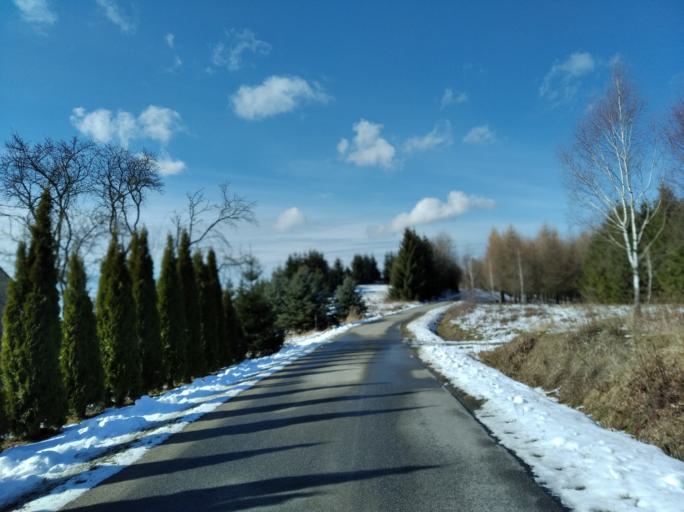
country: PL
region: Subcarpathian Voivodeship
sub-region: Powiat krosnienski
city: Korczyna
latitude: 49.7367
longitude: 21.8426
